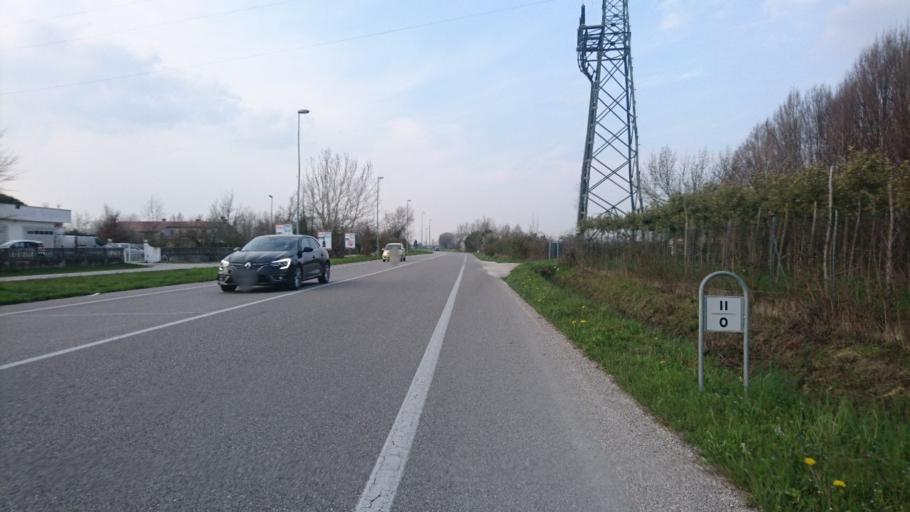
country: IT
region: Veneto
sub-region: Provincia di Padova
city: San Biagio
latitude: 45.3737
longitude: 11.7331
